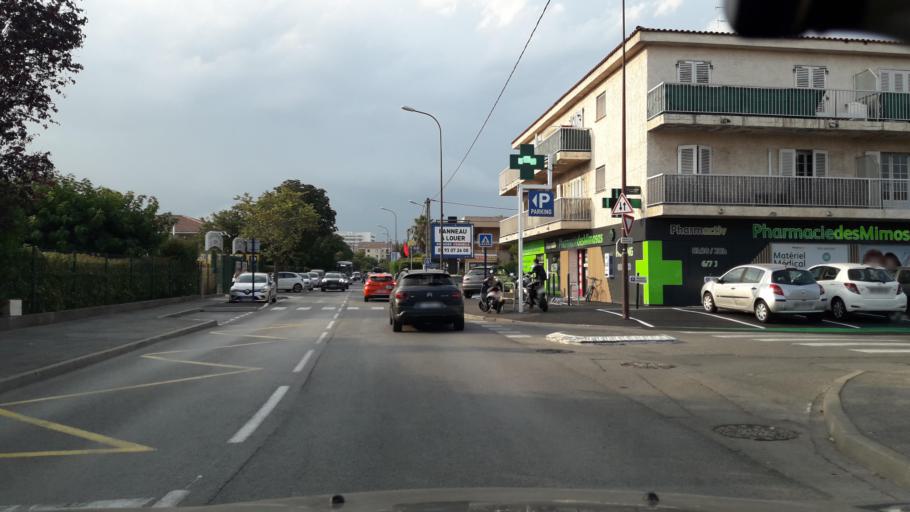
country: FR
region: Provence-Alpes-Cote d'Azur
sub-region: Departement du Var
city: Frejus
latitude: 43.4328
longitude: 6.7545
